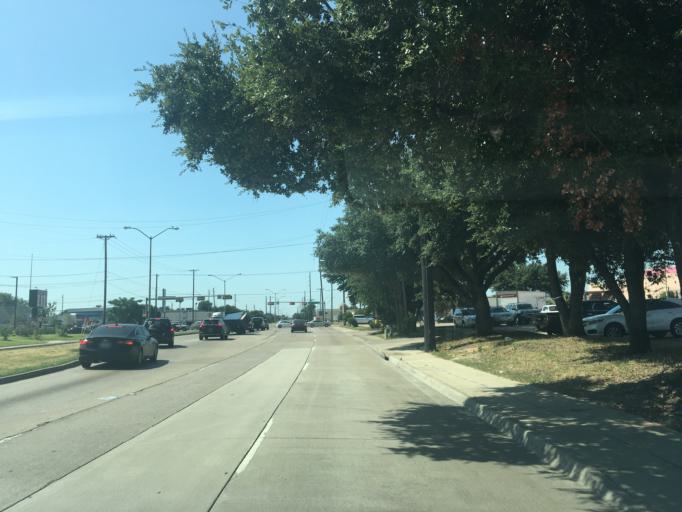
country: US
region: Texas
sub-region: Dallas County
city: Garland
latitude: 32.8652
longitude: -96.6658
